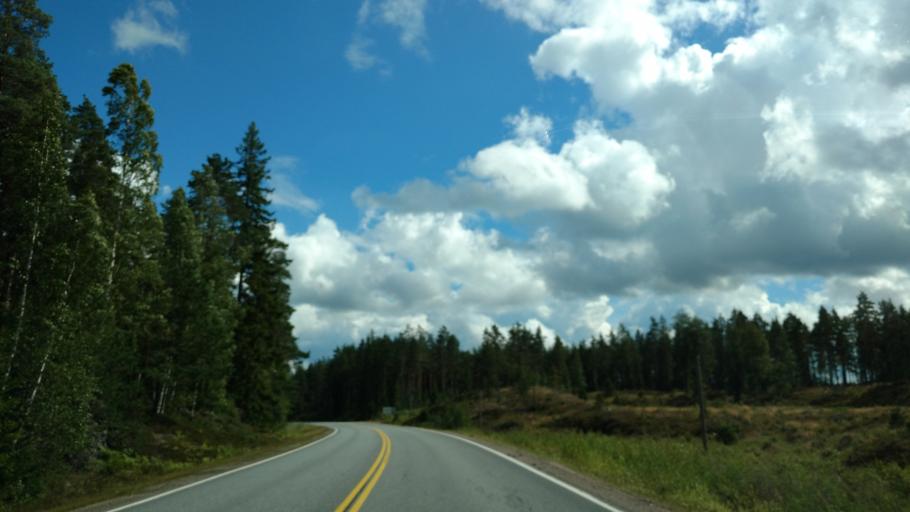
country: FI
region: Varsinais-Suomi
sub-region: Salo
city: Kisko
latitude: 60.2350
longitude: 23.5875
